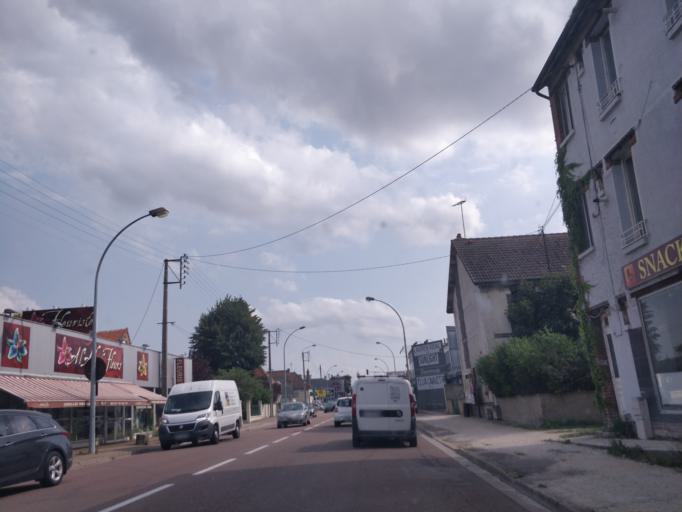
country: FR
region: Champagne-Ardenne
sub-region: Departement de l'Aube
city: Saint-Julien-les-Villas
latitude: 48.2764
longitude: 4.0831
